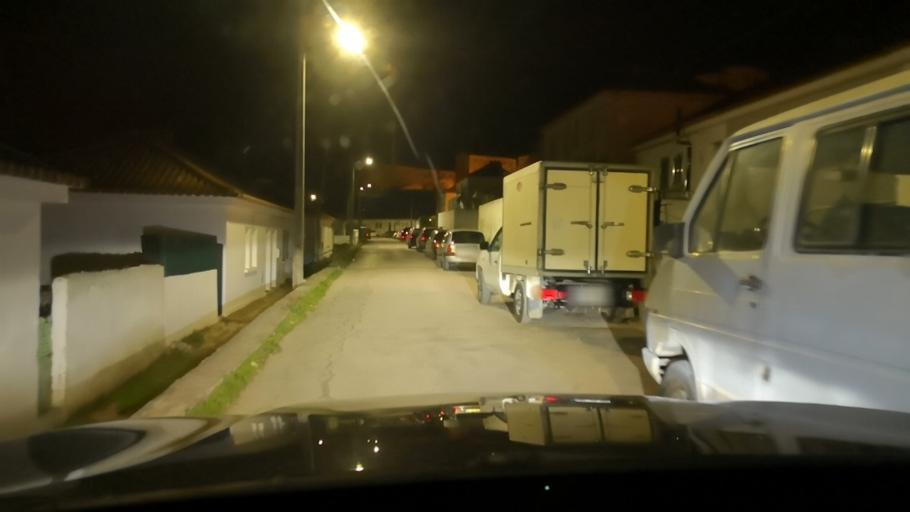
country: PT
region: Setubal
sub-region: Setubal
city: Setubal
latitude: 38.5283
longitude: -8.9033
